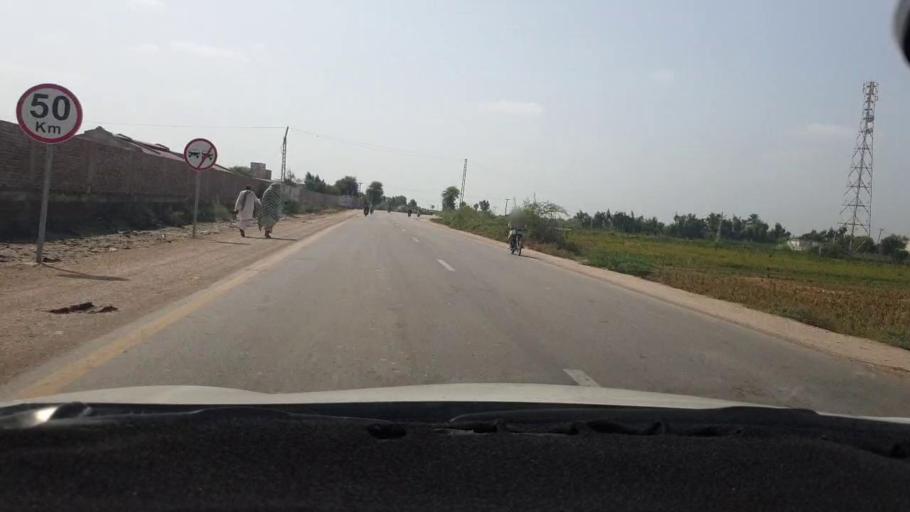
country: PK
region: Sindh
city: Mirpur Khas
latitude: 25.5726
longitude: 69.0694
